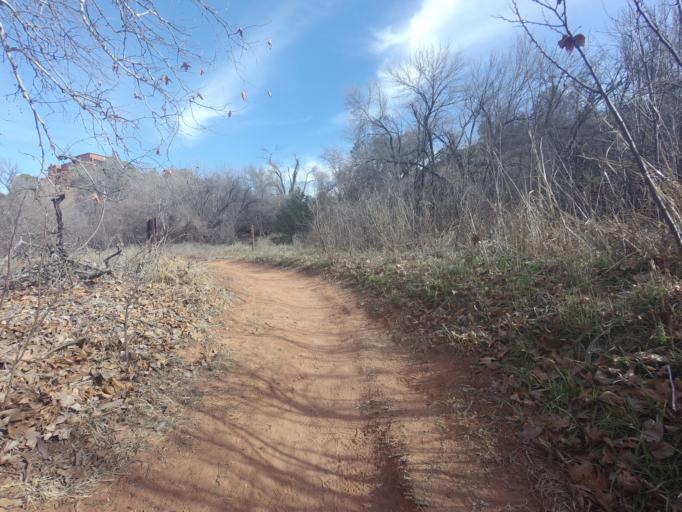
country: US
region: Arizona
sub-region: Yavapai County
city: West Sedona
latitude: 34.8087
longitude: -111.8272
